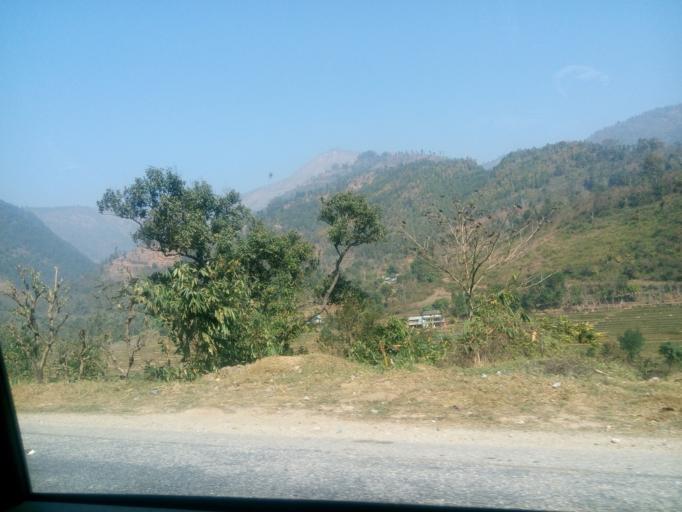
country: NP
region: Central Region
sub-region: Narayani Zone
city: Bharatpur
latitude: 27.8132
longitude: 84.8135
